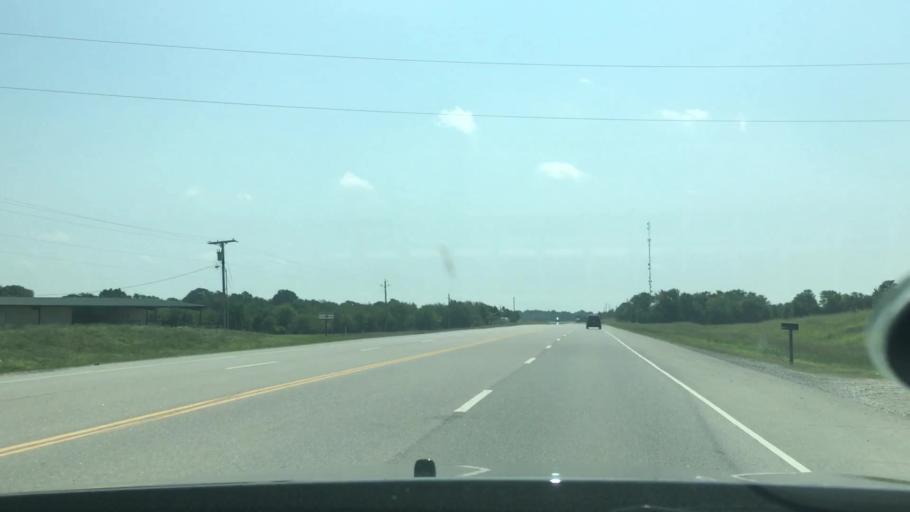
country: US
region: Oklahoma
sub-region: Atoka County
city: Atoka
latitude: 34.3630
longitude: -96.0983
